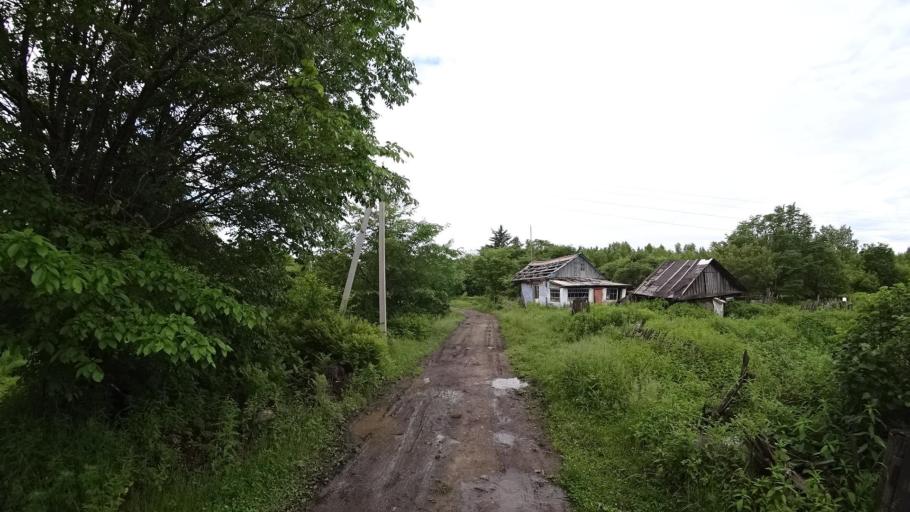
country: RU
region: Khabarovsk Krai
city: Amursk
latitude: 49.9061
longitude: 136.1328
